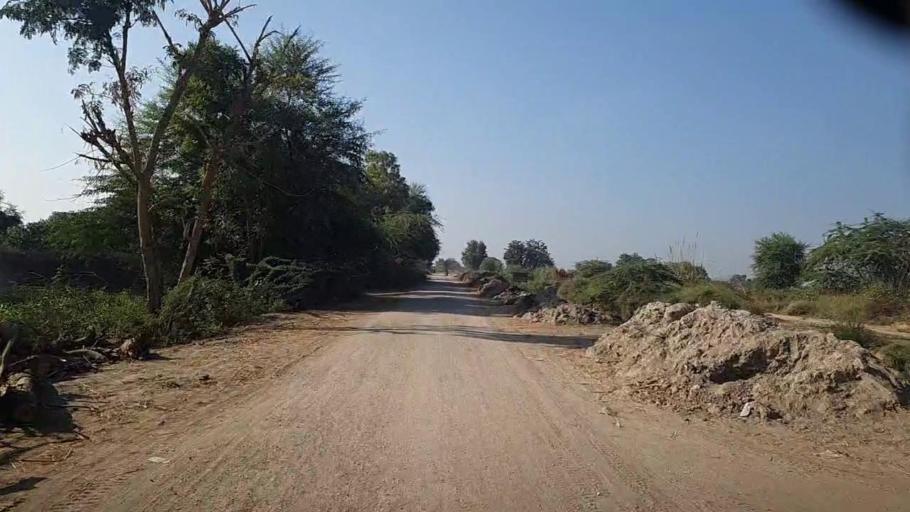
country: PK
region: Sindh
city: Darya Khan Marri
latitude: 26.6797
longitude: 68.3694
